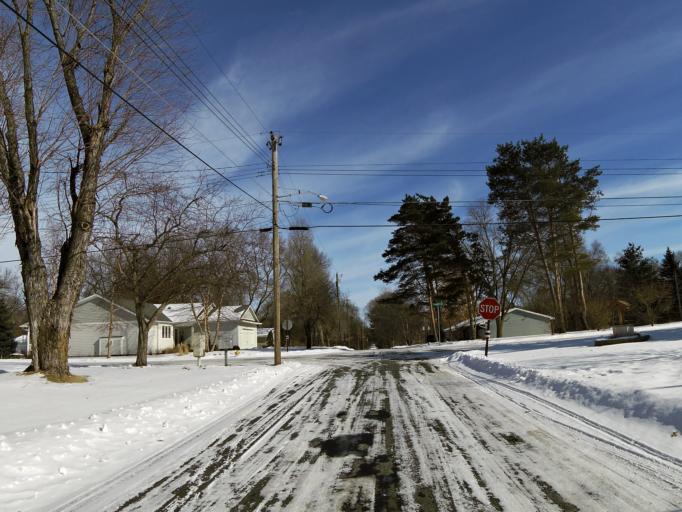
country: US
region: Minnesota
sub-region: Washington County
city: Lake Saint Croix Beach
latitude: 44.9229
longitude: -92.7691
